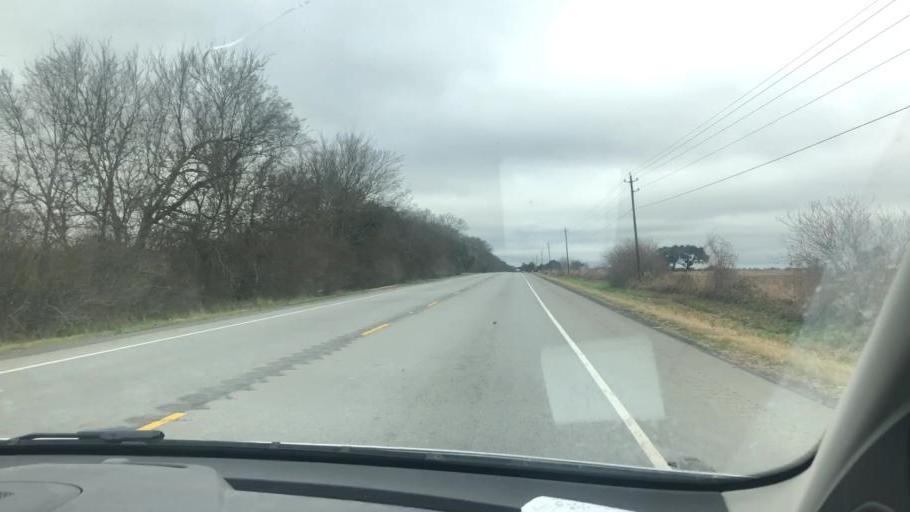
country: US
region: Texas
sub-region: Matagorda County
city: Bay City
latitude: 29.0770
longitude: -95.9728
